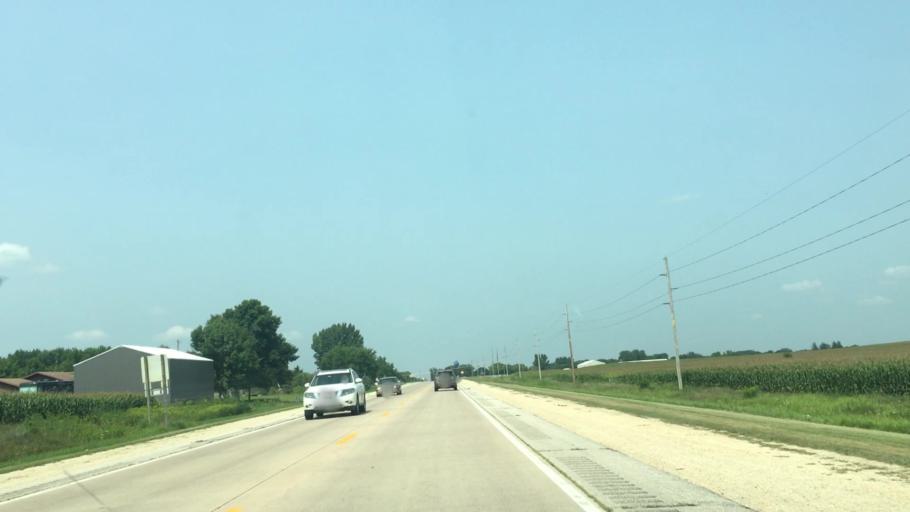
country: US
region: Iowa
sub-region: Fayette County
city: Oelwein
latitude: 42.6054
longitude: -91.9030
